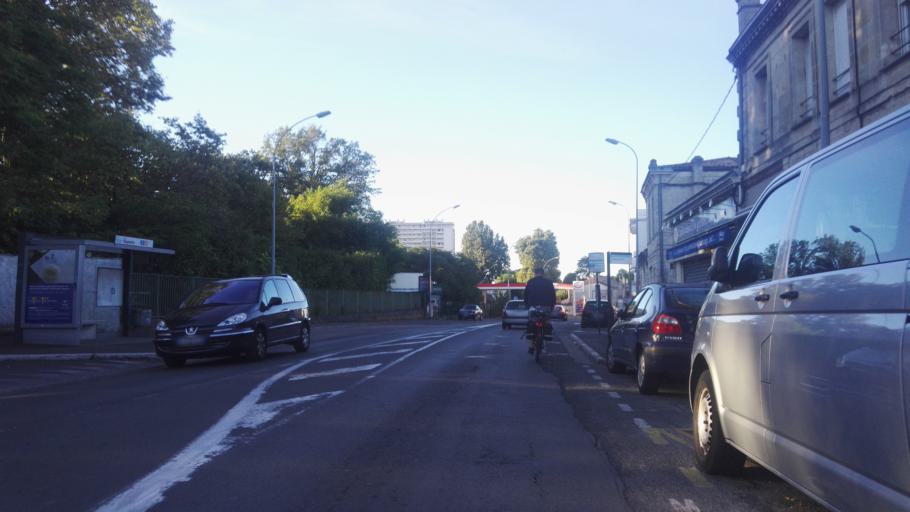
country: FR
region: Aquitaine
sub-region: Departement de la Gironde
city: Talence
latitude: 44.8084
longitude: -0.5737
